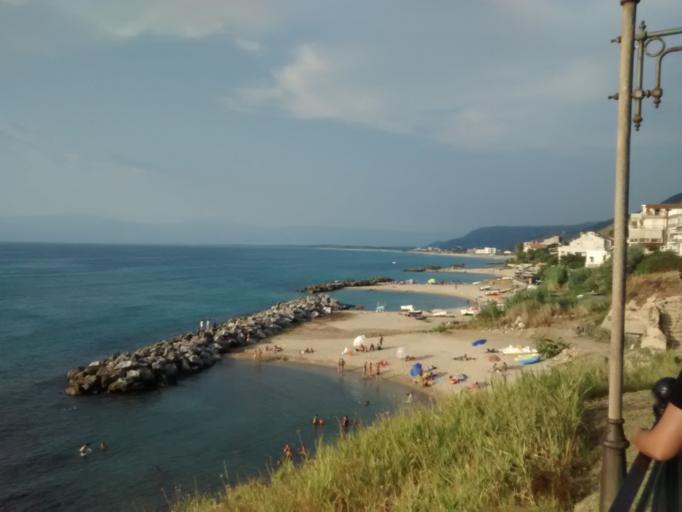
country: IT
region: Calabria
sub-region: Provincia di Vibo-Valentia
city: Pizzo
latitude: 38.7419
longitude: 16.1744
